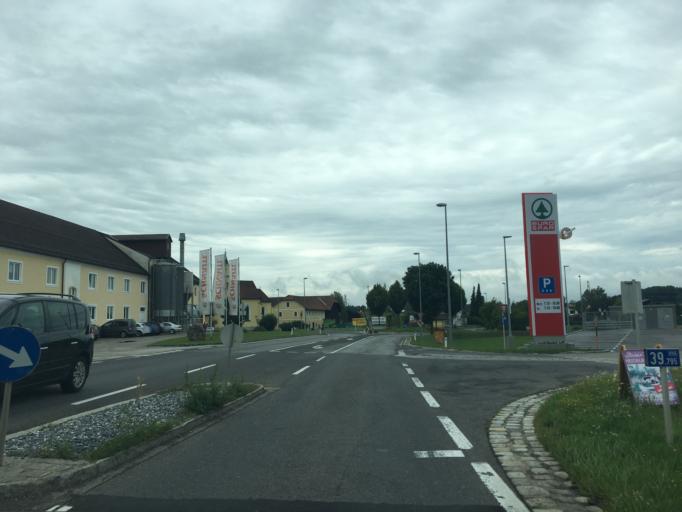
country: AT
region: Salzburg
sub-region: Politischer Bezirk Salzburg-Umgebung
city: Dorfbeuern
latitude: 48.0894
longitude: 12.9914
